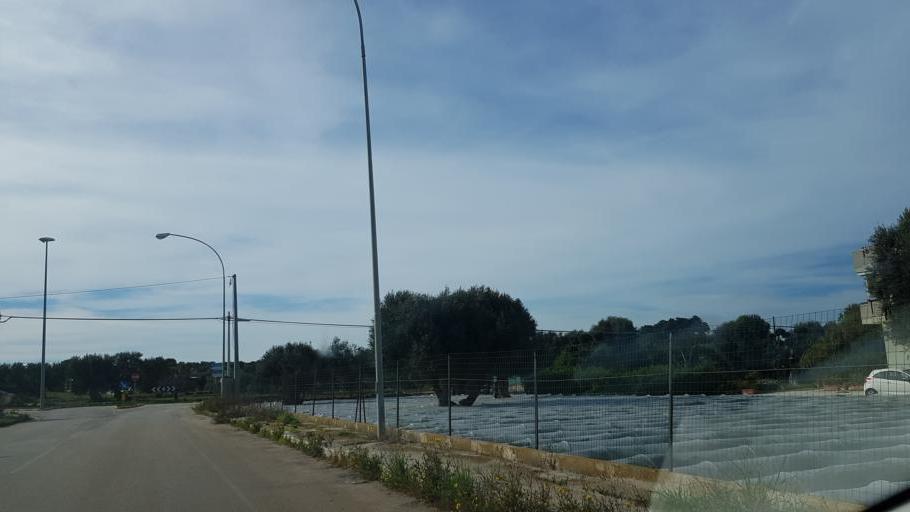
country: IT
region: Apulia
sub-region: Provincia di Brindisi
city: Fasano
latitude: 40.8994
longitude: 17.3539
